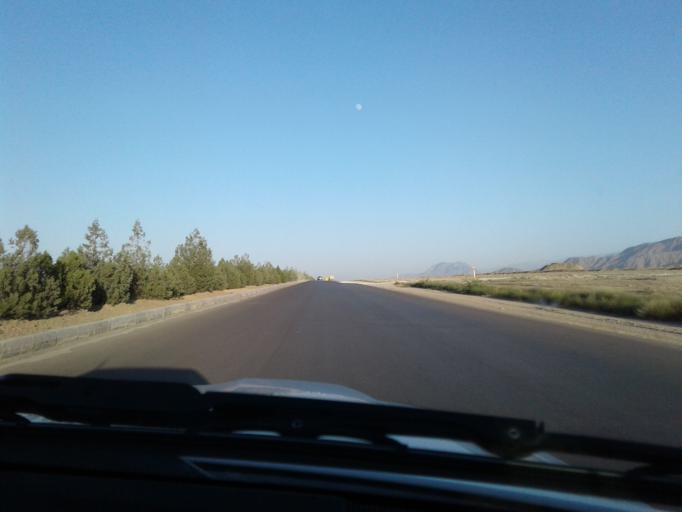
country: TM
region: Ahal
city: Baharly
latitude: 38.2346
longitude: 57.7781
